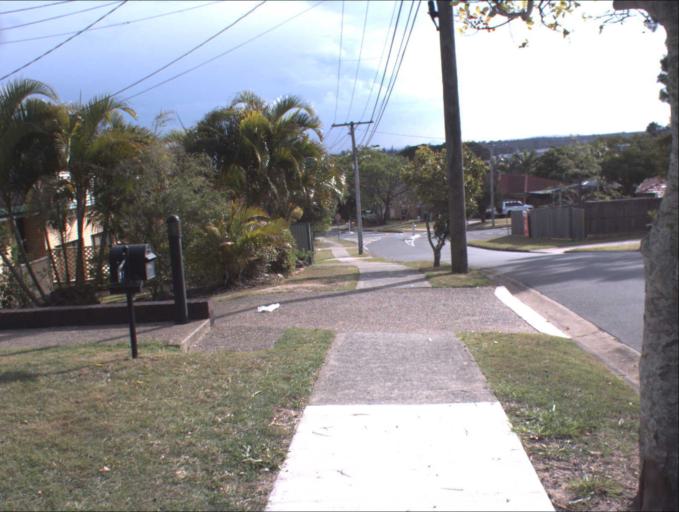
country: AU
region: Queensland
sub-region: Logan
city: Springwood
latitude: -27.6125
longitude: 153.1323
